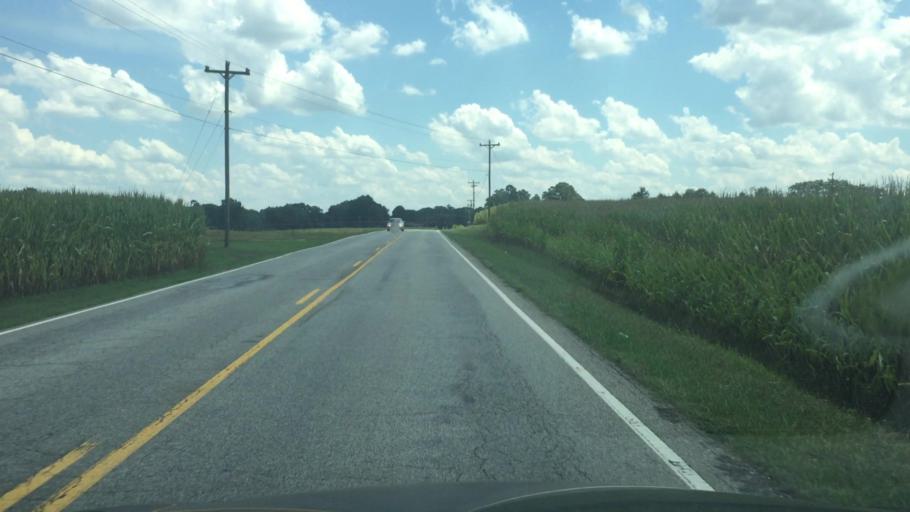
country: US
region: North Carolina
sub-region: Rowan County
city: Enochville
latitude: 35.5761
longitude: -80.6546
